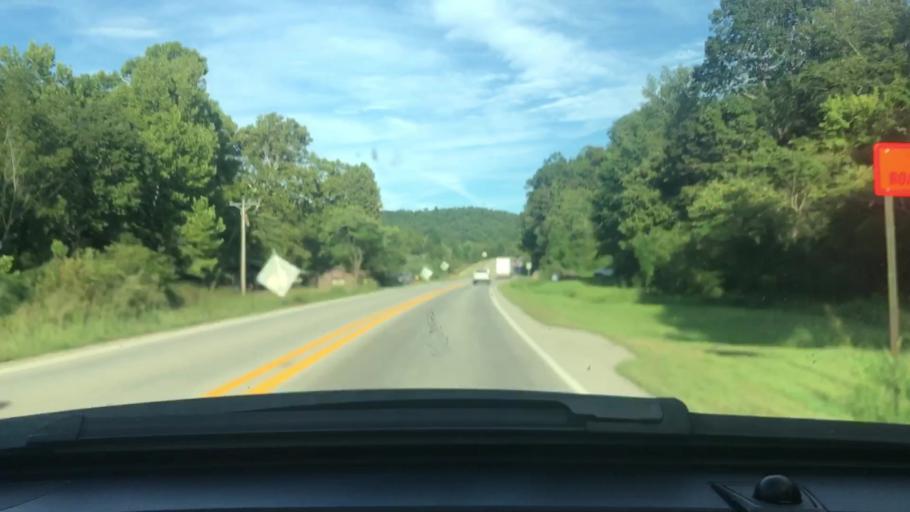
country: US
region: Arkansas
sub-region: Sharp County
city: Cherokee Village
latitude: 36.3037
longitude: -91.4227
